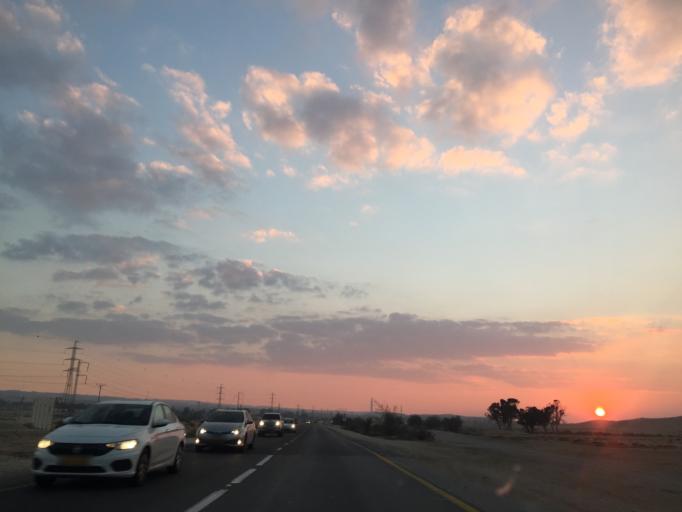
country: IL
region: Southern District
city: Yeroham
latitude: 31.0219
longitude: 34.7920
